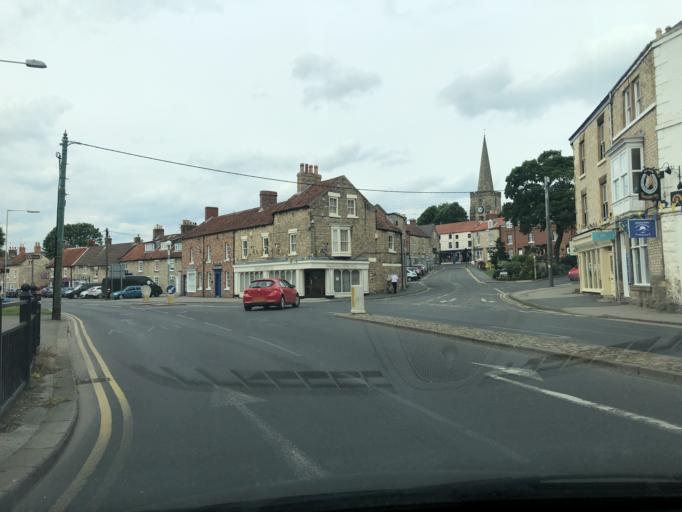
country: GB
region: England
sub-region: North Yorkshire
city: Pickering
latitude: 54.2441
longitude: -0.7752
